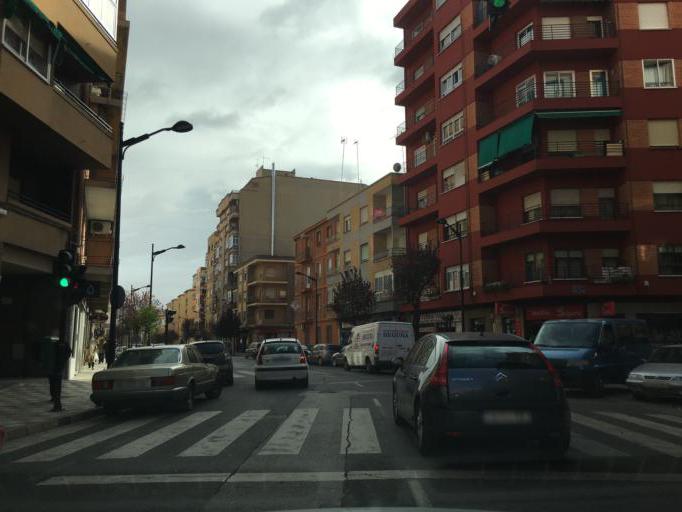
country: ES
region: Castille-La Mancha
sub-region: Provincia de Albacete
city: Albacete
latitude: 38.9897
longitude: -1.8657
